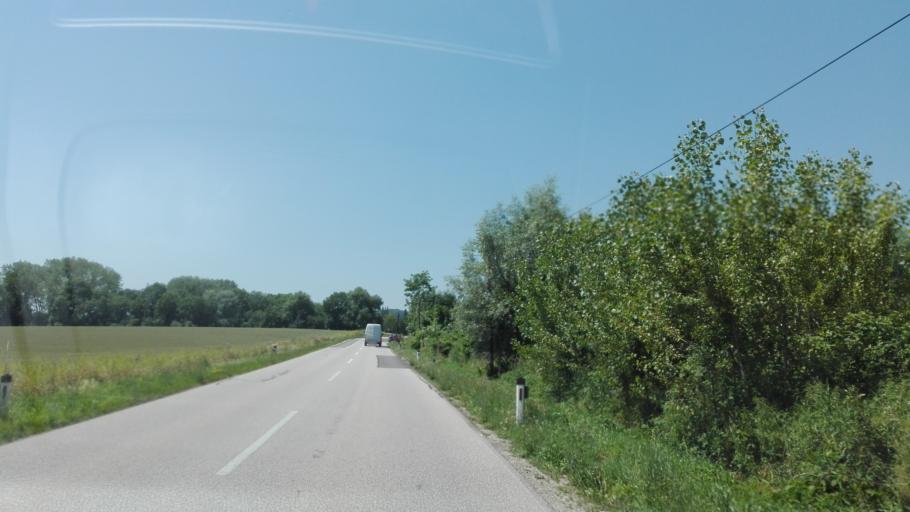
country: AT
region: Upper Austria
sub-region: Politischer Bezirk Linz-Land
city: Pasching
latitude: 48.2704
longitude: 14.2087
